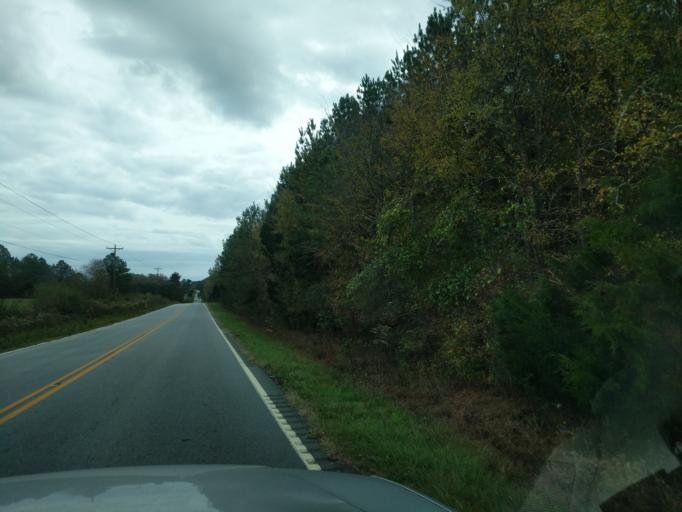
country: US
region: South Carolina
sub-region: Saluda County
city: Saluda
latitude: 34.0270
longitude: -81.7979
